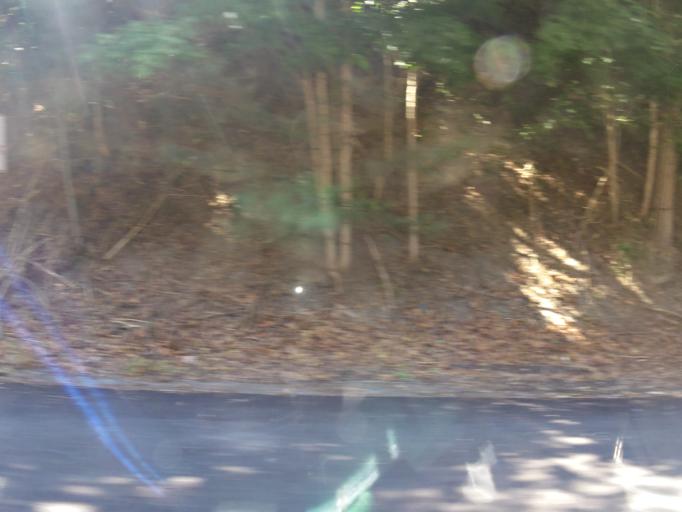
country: US
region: Kentucky
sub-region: Leslie County
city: Hyden
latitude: 37.1605
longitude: -83.3717
